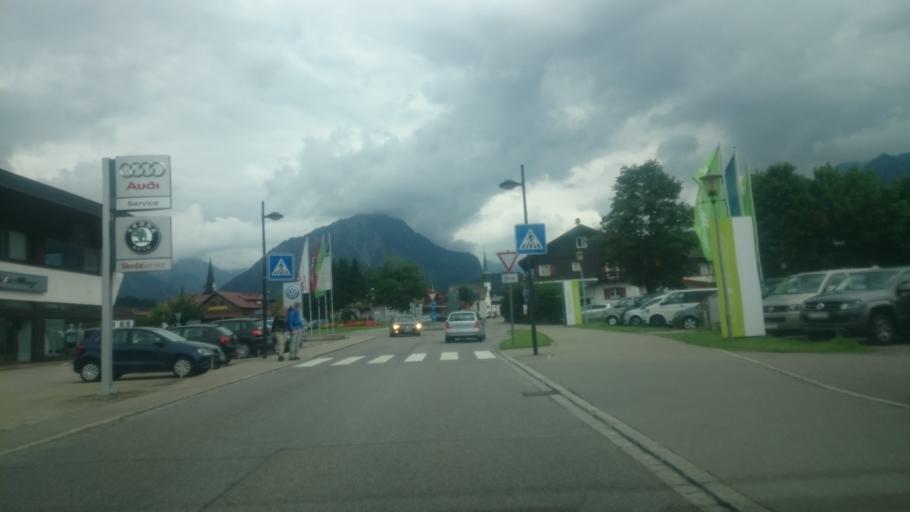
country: DE
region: Bavaria
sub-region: Swabia
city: Oberstdorf
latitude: 47.4130
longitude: 10.2754
